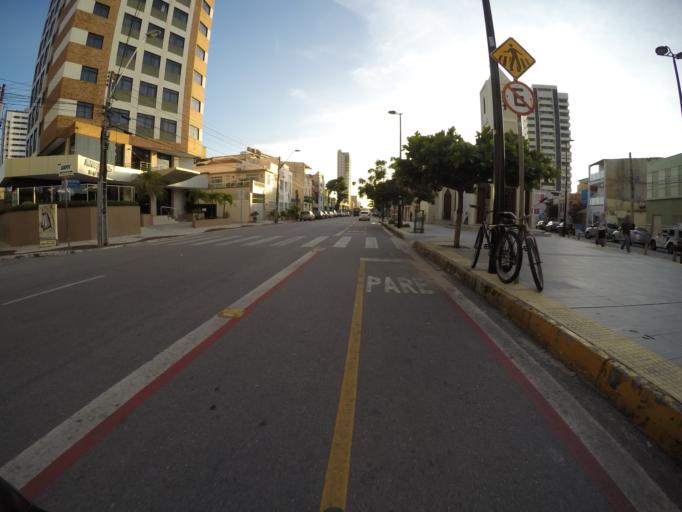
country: BR
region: Ceara
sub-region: Fortaleza
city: Fortaleza
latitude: -3.7199
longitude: -38.5134
